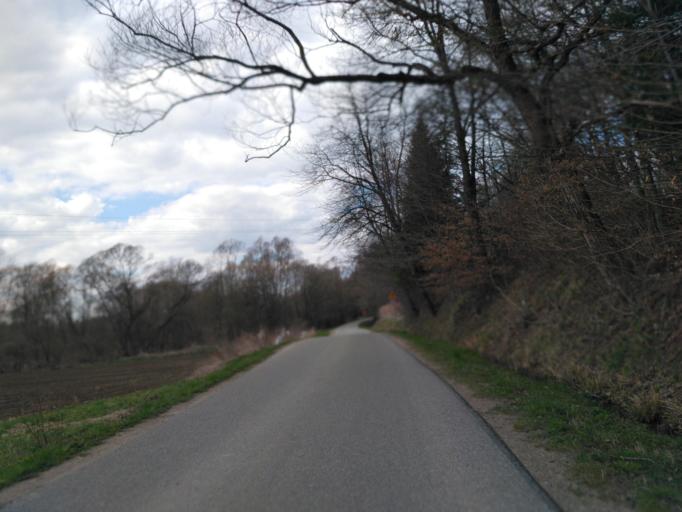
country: PL
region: Subcarpathian Voivodeship
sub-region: Powiat sanocki
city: Tyrawa Woloska
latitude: 49.6602
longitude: 22.3000
